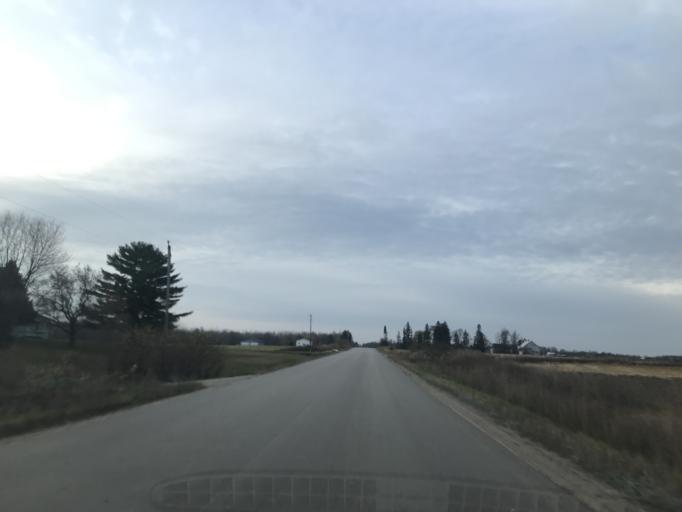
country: US
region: Wisconsin
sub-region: Marinette County
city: Peshtigo
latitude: 45.0820
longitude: -87.7996
